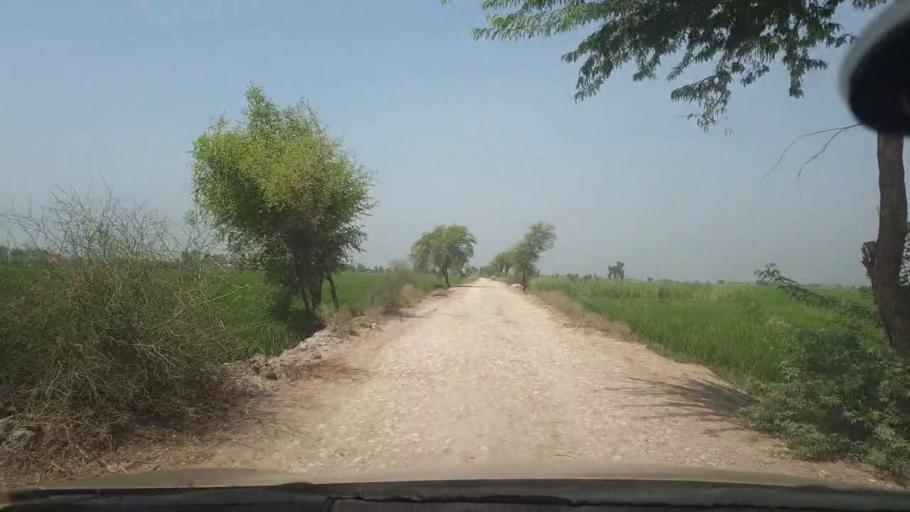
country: PK
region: Sindh
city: Shahdadkot
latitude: 27.7569
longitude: 67.9445
